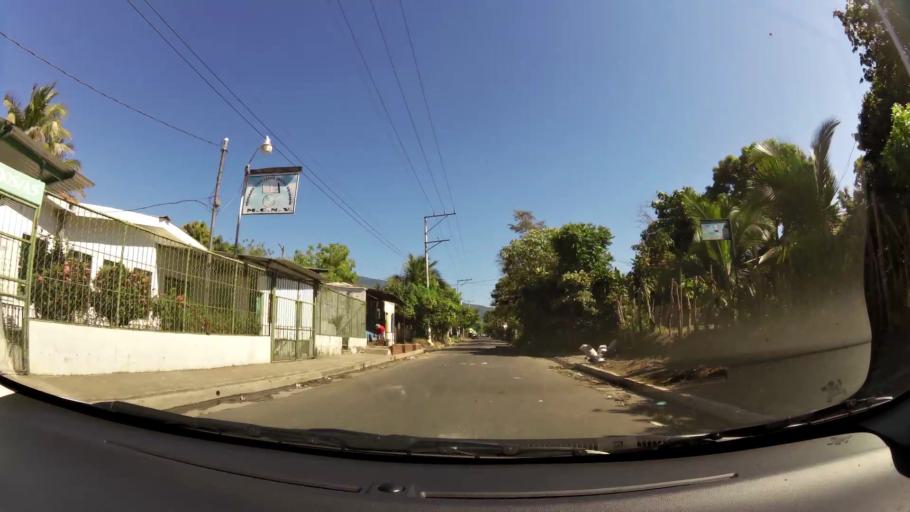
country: SV
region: La Libertad
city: Santa Tecla
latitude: 13.7339
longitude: -89.3799
